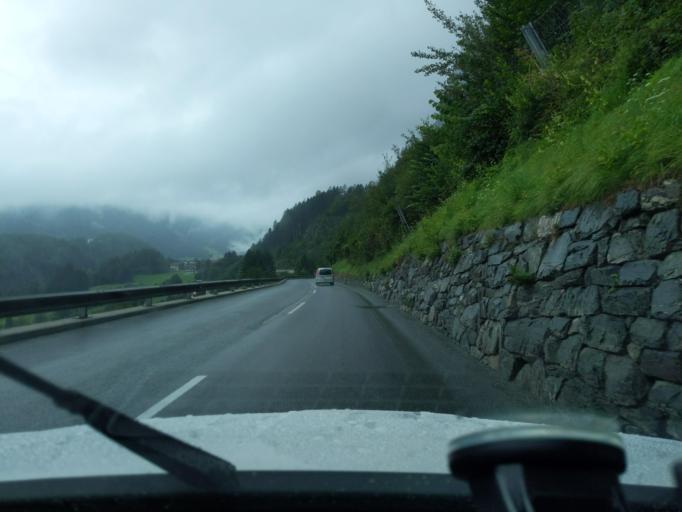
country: AT
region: Tyrol
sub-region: Politischer Bezirk Schwaz
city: Mayrhofen
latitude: 47.1603
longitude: 11.8385
